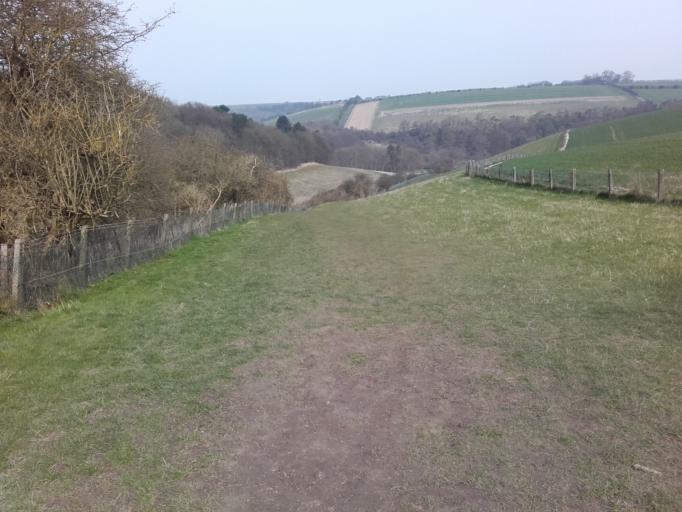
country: GB
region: England
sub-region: East Riding of Yorkshire
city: South Cave
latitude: 53.7810
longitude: -0.5786
